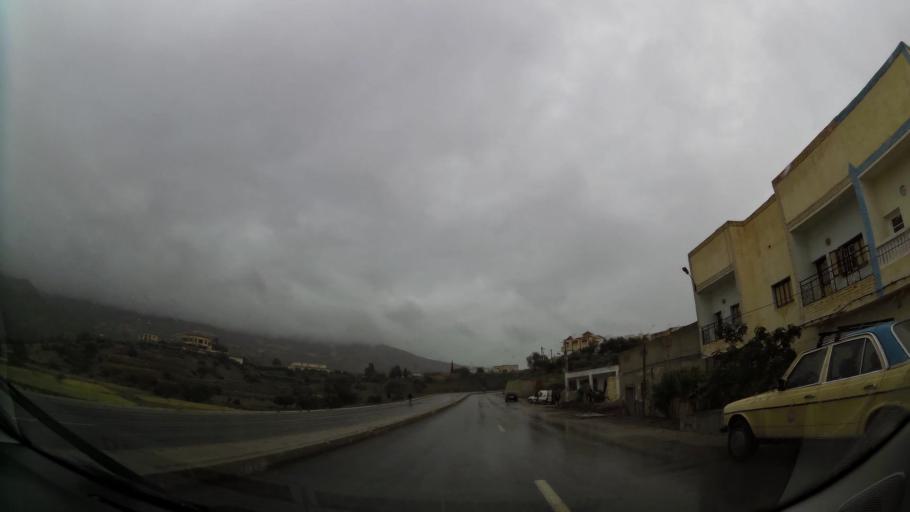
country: MA
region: Taza-Al Hoceima-Taounate
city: Imzourene
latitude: 35.0415
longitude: -3.8224
